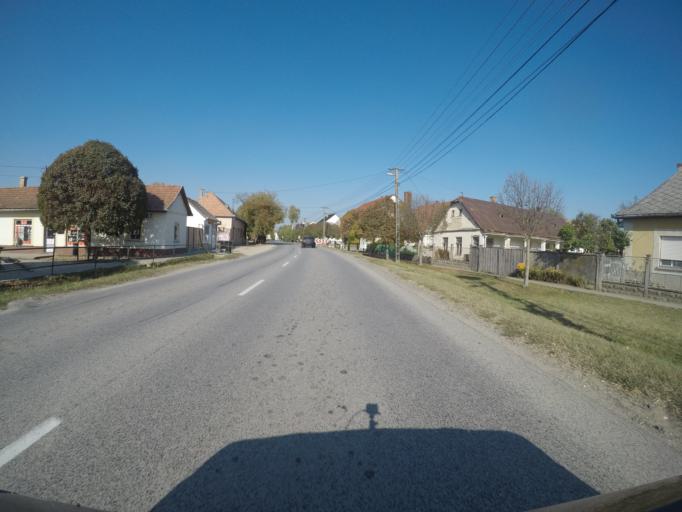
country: HU
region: Tolna
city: Nagydorog
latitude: 46.6226
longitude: 18.6561
